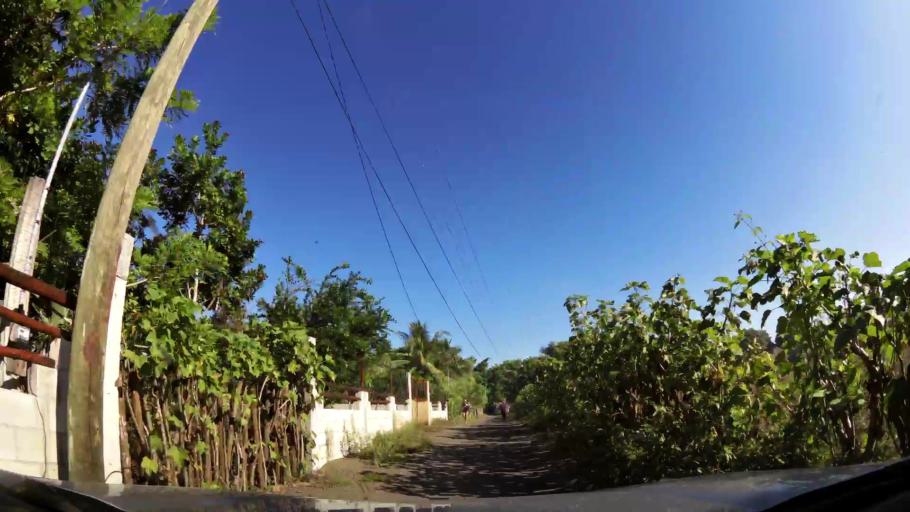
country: GT
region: Santa Rosa
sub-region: Municipio de Taxisco
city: Taxisco
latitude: 13.8943
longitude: -90.4905
